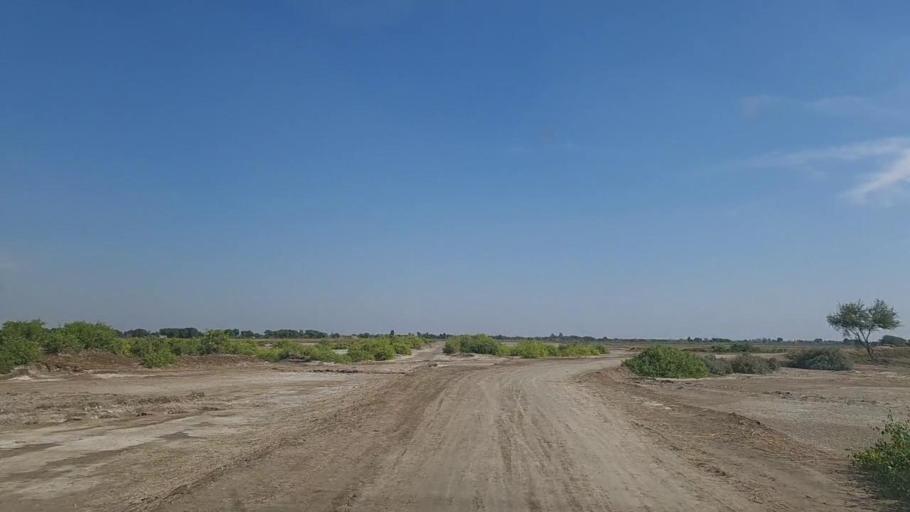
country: PK
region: Sindh
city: Mirpur Batoro
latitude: 24.7612
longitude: 68.2959
